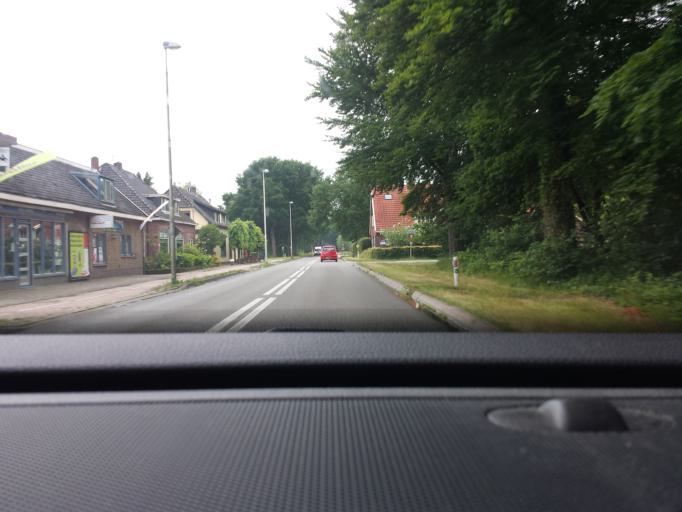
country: NL
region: Gelderland
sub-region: Gemeente Lochem
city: Barchem
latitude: 52.0973
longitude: 6.3887
